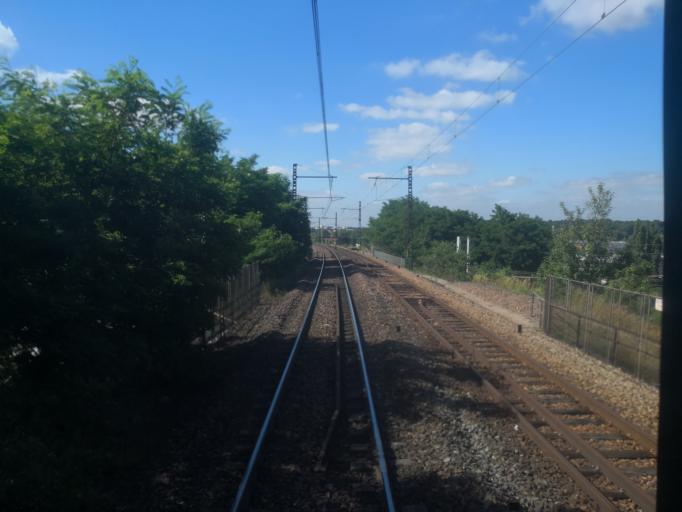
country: FR
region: Ile-de-France
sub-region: Departement de Seine-et-Marne
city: La Rochette
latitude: 48.5193
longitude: 2.6659
